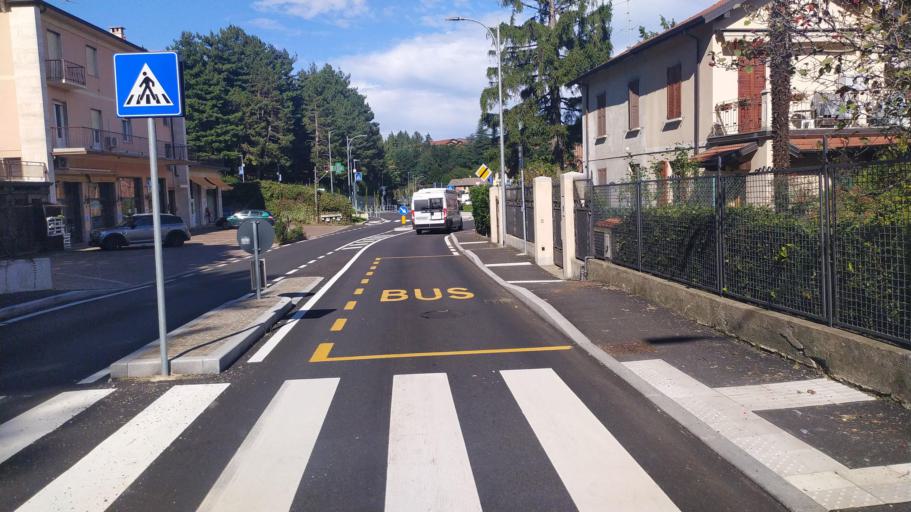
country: IT
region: Lombardy
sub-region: Provincia di Varese
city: Gazzada Schianno
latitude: 45.7998
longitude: 8.8336
